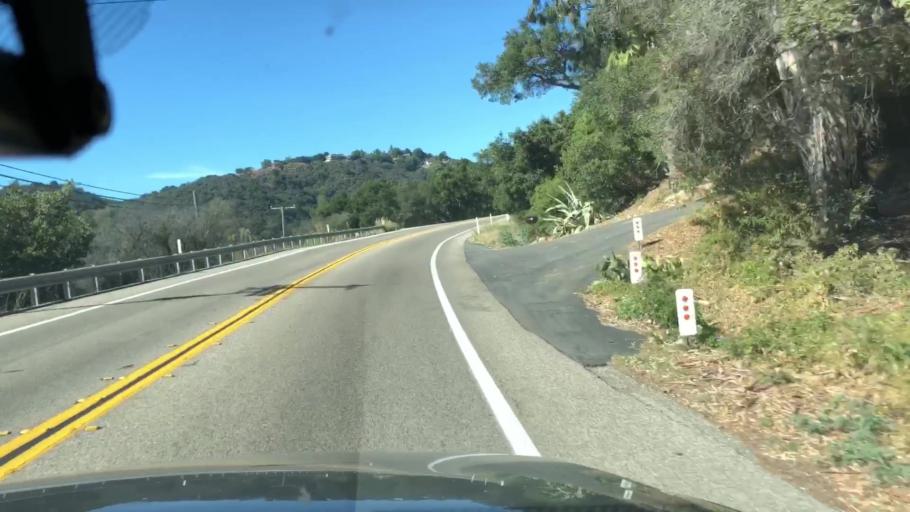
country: US
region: California
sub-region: Santa Barbara County
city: Goleta
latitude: 34.4924
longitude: -119.7978
